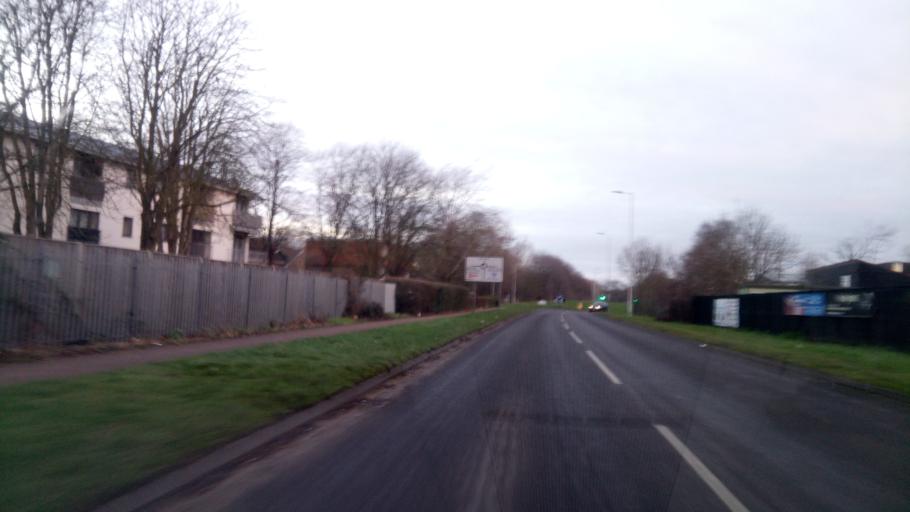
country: GB
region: England
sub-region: Peterborough
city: Peterborough
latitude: 52.5827
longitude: -0.2654
